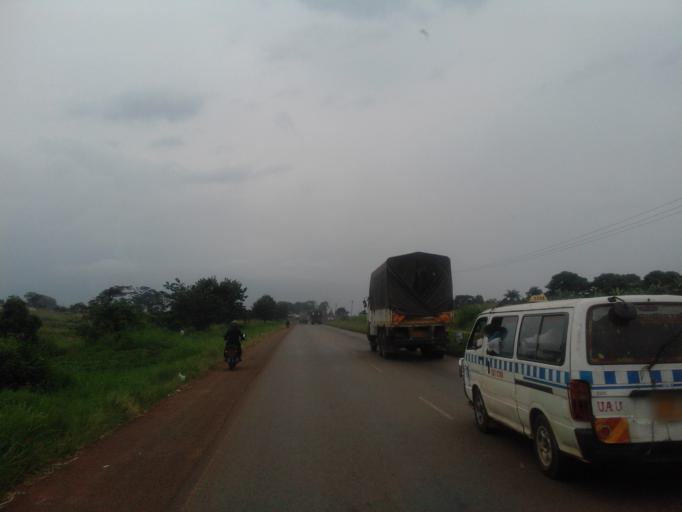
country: UG
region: Eastern Region
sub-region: Jinja District
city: Jinja
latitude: 0.4438
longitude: 33.2070
